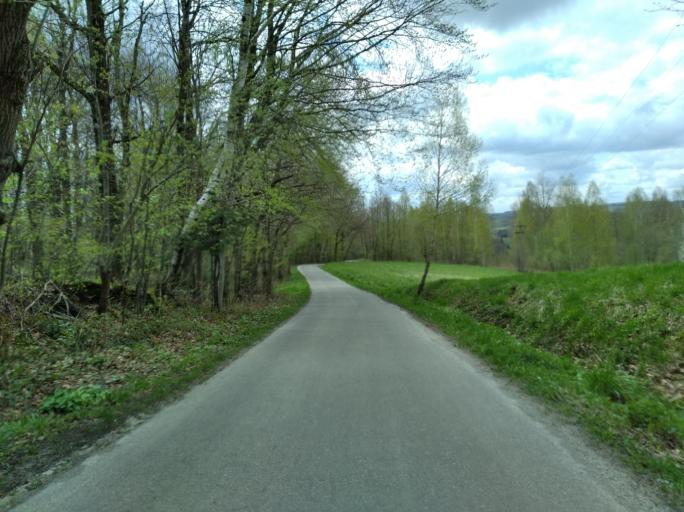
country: PL
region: Subcarpathian Voivodeship
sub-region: Powiat strzyzowski
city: Niebylec
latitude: 49.8842
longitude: 21.9250
